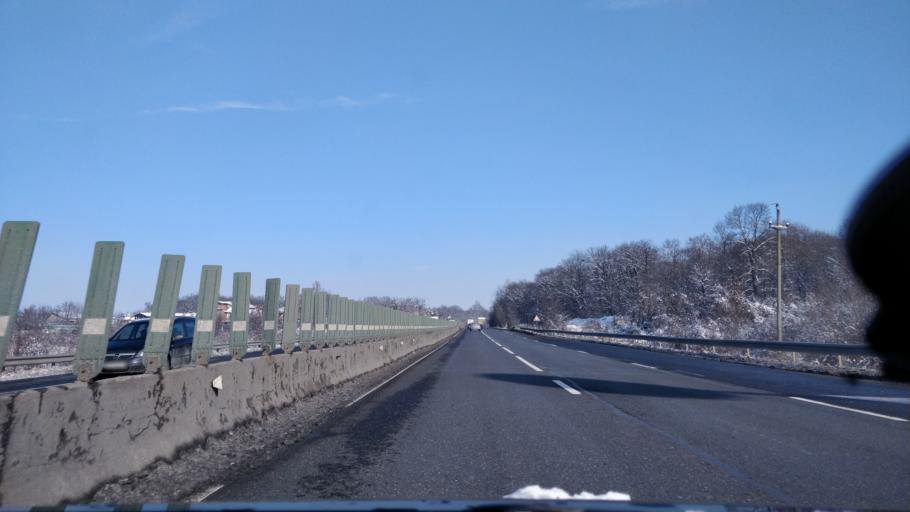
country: RO
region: Ilfov
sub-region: Comuna Mogosoaia
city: Mogosoaia
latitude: 44.5105
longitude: 26.0080
